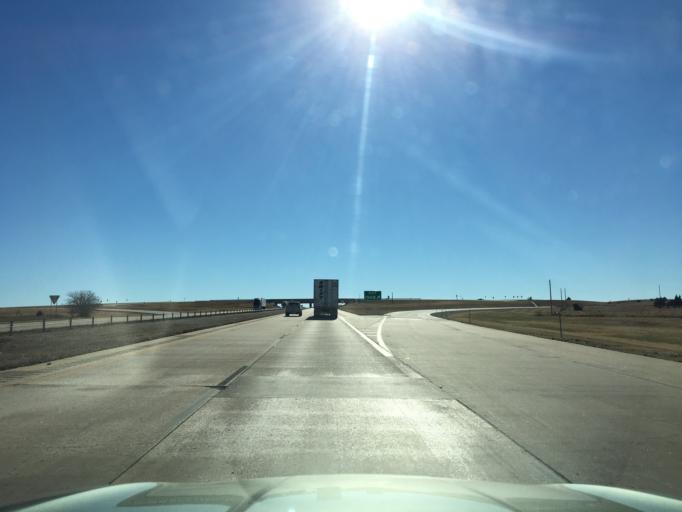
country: US
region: Oklahoma
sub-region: Noble County
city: Perry
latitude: 36.4049
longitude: -97.3272
